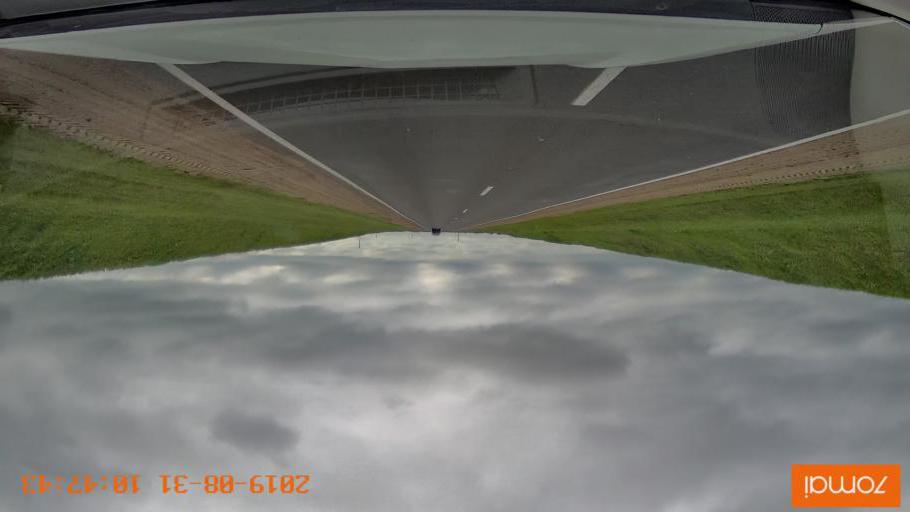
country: BY
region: Mogilev
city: Palykavichy Pyershyya
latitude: 53.9868
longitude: 30.4324
